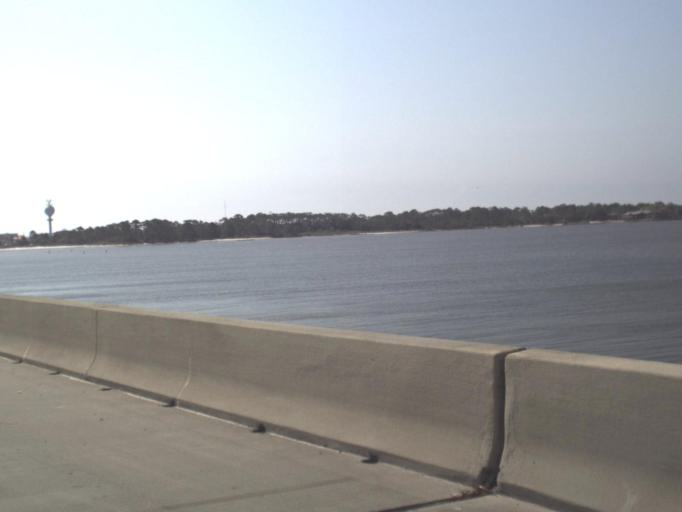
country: US
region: Florida
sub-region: Franklin County
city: Eastpoint
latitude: 29.6720
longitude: -84.8682
